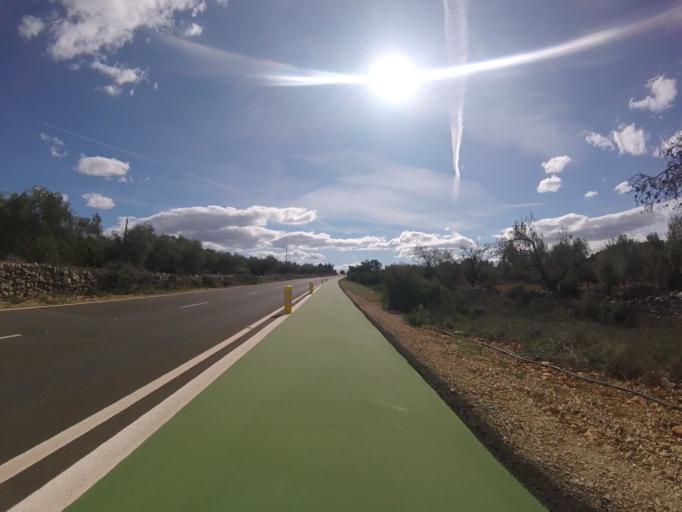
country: ES
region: Valencia
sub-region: Provincia de Castello
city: Albocasser
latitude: 40.4140
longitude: 0.0711
